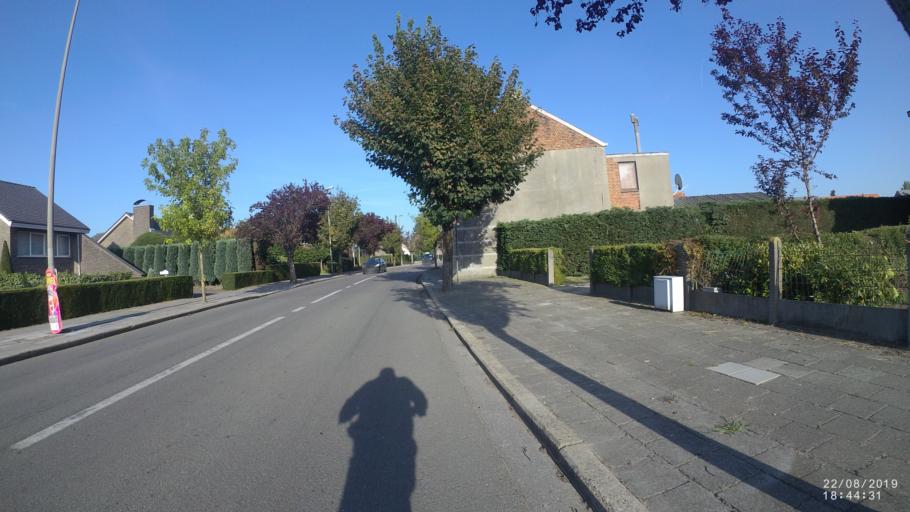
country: BE
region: Flanders
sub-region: Provincie Oost-Vlaanderen
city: Eeklo
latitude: 51.1931
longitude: 3.5632
